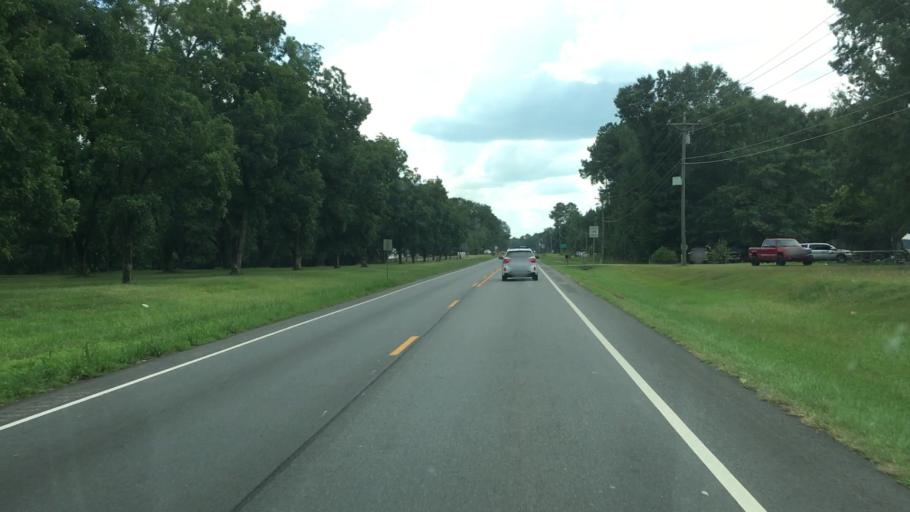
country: US
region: Georgia
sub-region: Putnam County
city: Eatonton
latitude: 33.3635
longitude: -83.3861
